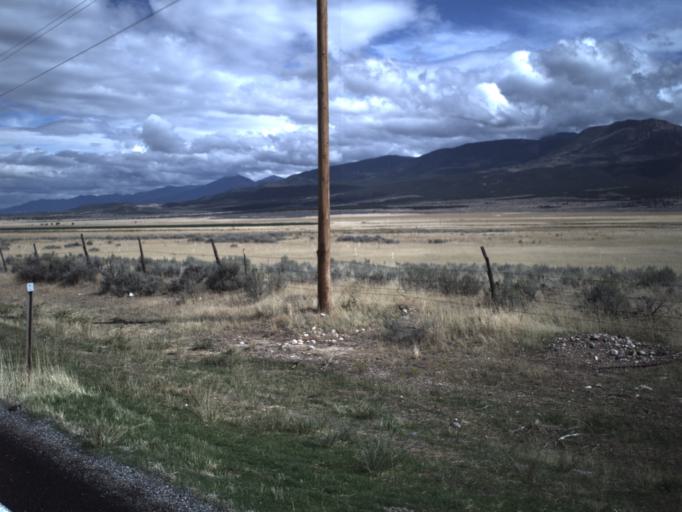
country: US
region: Utah
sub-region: Millard County
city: Fillmore
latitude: 38.8203
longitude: -112.4338
